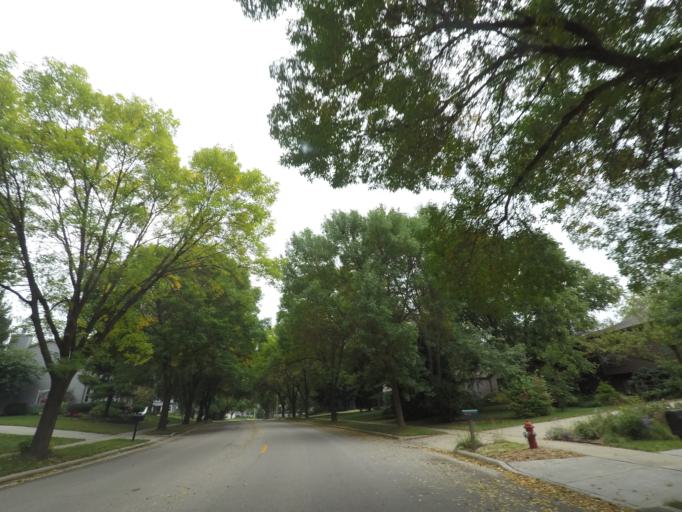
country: US
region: Wisconsin
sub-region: Dane County
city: Middleton
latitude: 43.0848
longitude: -89.5116
